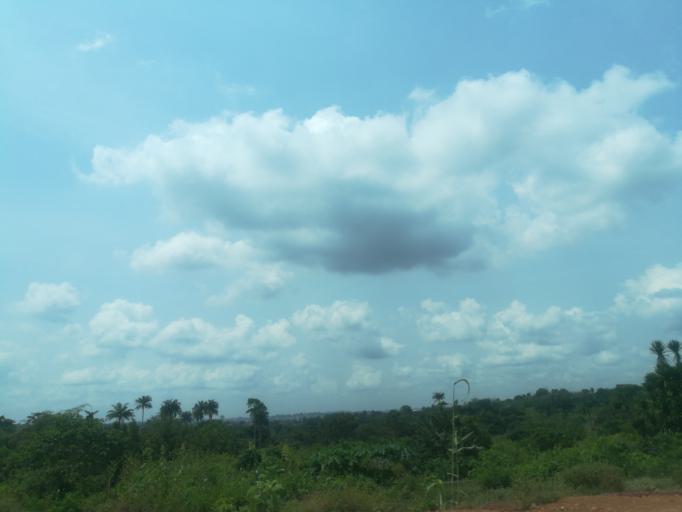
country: NG
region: Oyo
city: Moniya
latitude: 7.4522
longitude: 3.9496
